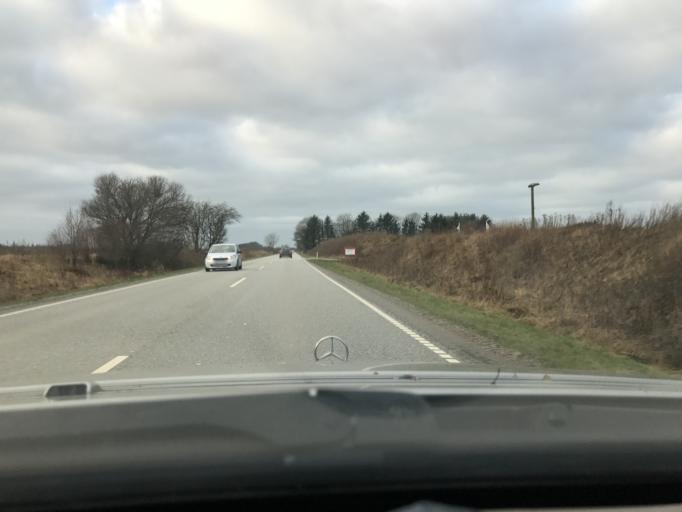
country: DK
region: South Denmark
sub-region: Aabenraa Kommune
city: Rodekro
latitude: 55.0746
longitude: 9.2957
